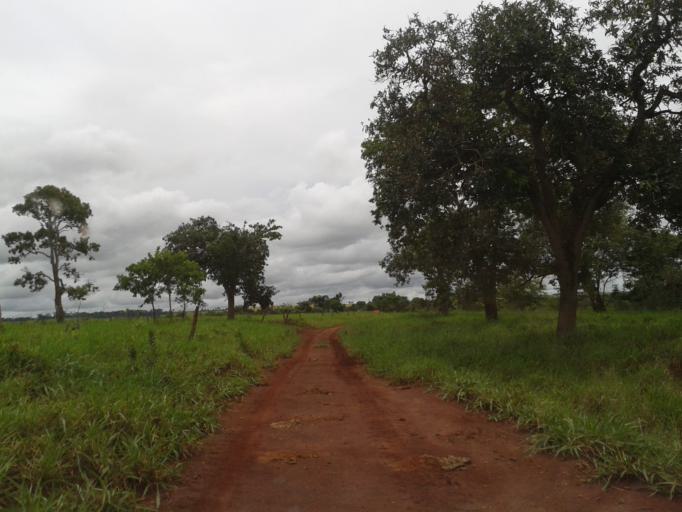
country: BR
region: Minas Gerais
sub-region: Capinopolis
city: Capinopolis
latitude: -18.7883
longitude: -49.7896
